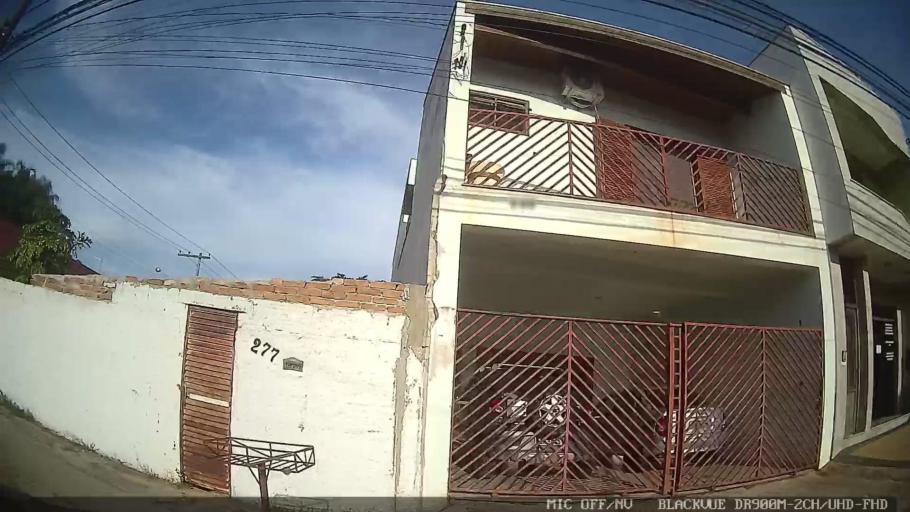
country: BR
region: Sao Paulo
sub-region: Tiete
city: Tiete
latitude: -23.0995
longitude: -47.7143
